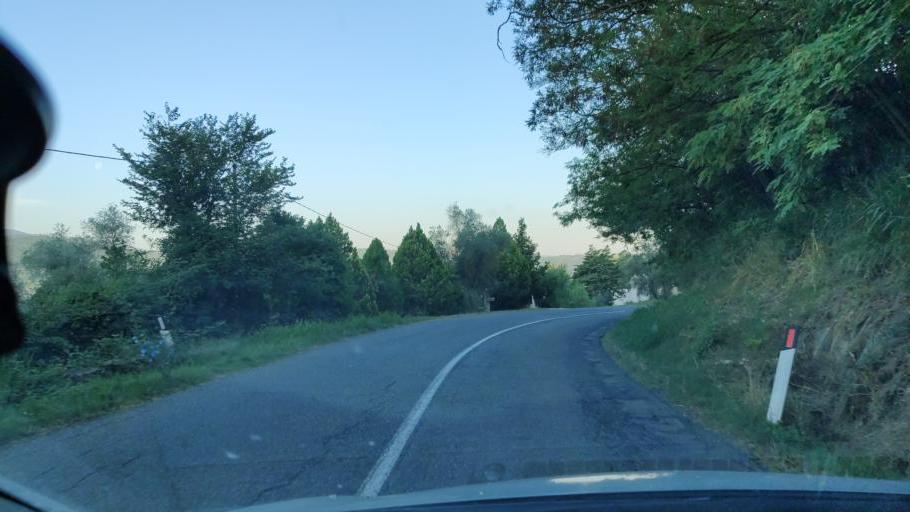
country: IT
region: Umbria
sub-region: Provincia di Terni
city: Giove
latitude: 42.5024
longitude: 12.3207
